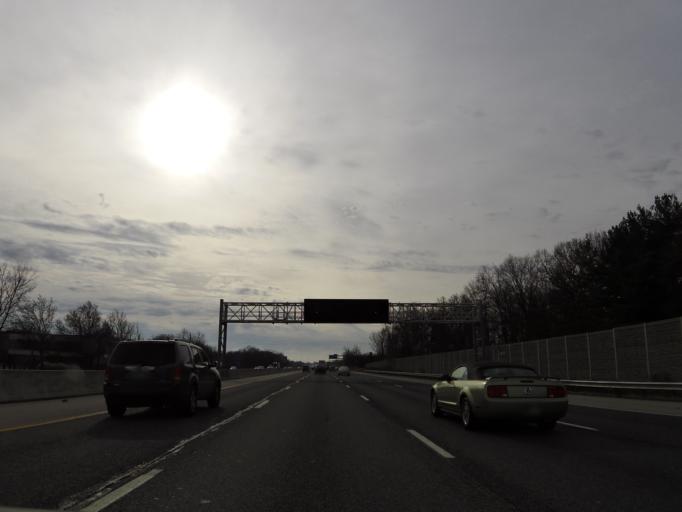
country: US
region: Indiana
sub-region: Marion County
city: Lawrence
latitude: 39.8779
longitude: -86.0474
